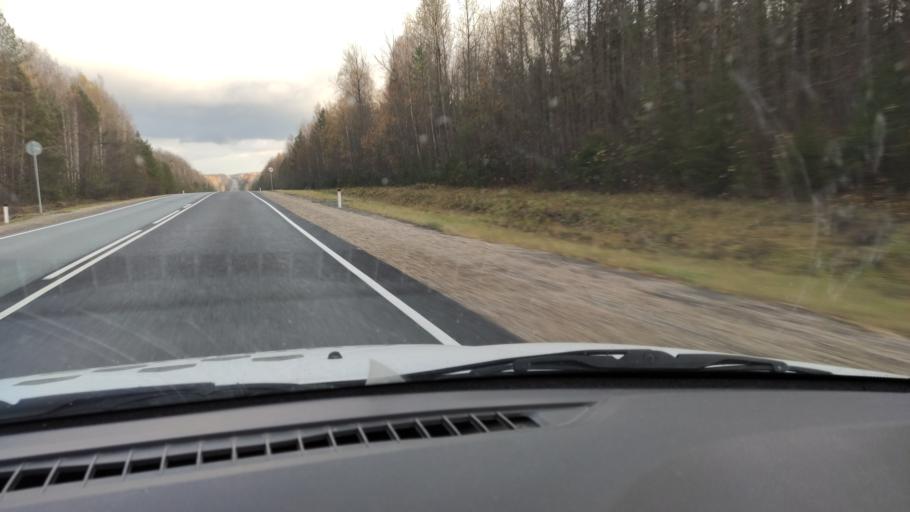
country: RU
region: Kirov
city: Chernaya Kholunitsa
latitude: 58.7975
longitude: 51.8701
